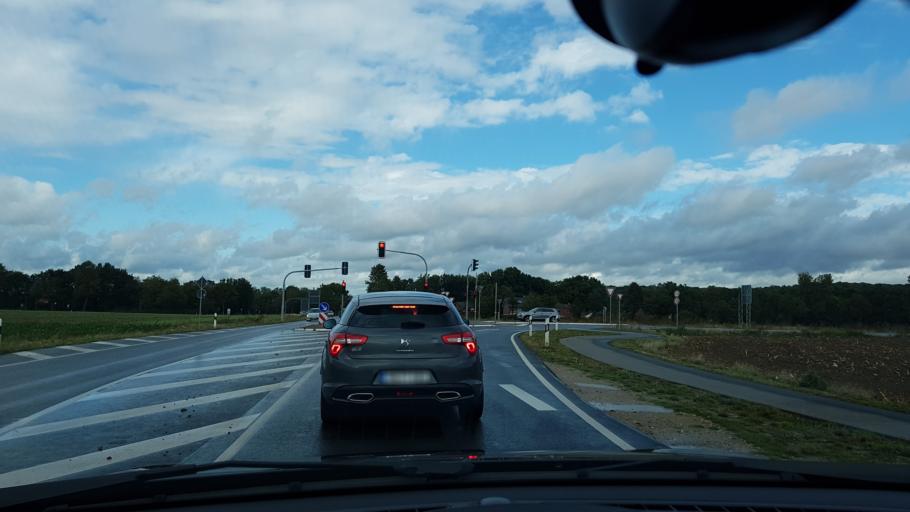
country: DE
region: North Rhine-Westphalia
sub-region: Regierungsbezirk Koln
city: Wassenberg
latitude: 51.0861
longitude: 6.1645
